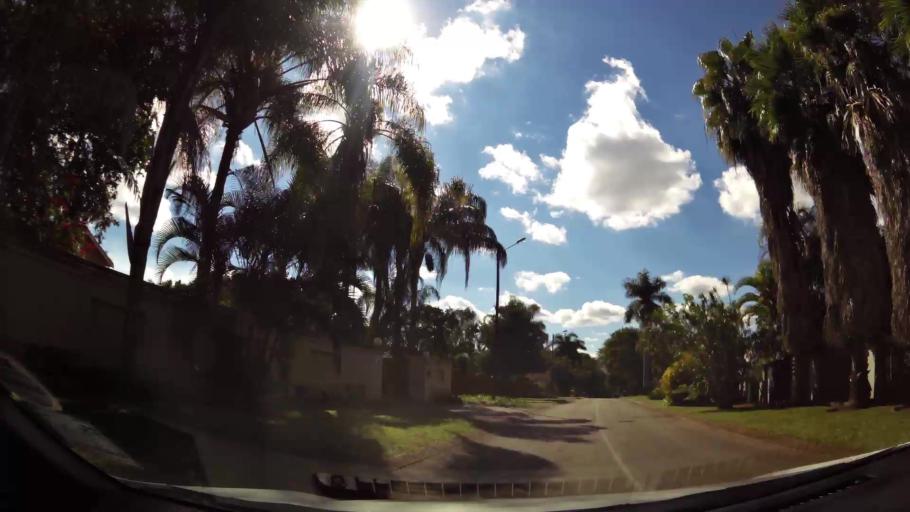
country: ZA
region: Limpopo
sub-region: Mopani District Municipality
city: Tzaneen
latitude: -23.8170
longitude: 30.1471
